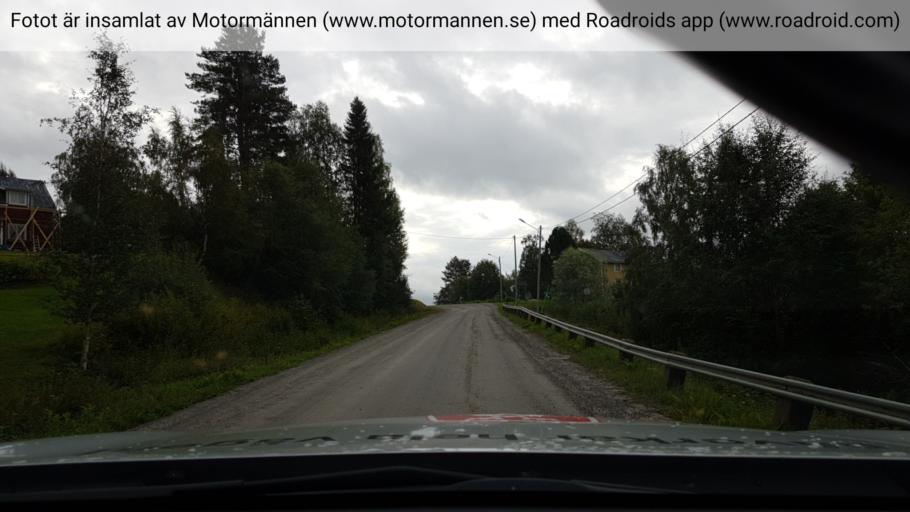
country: SE
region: Vaesterbotten
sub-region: Vannas Kommun
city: Vannasby
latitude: 64.0995
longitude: 20.0031
